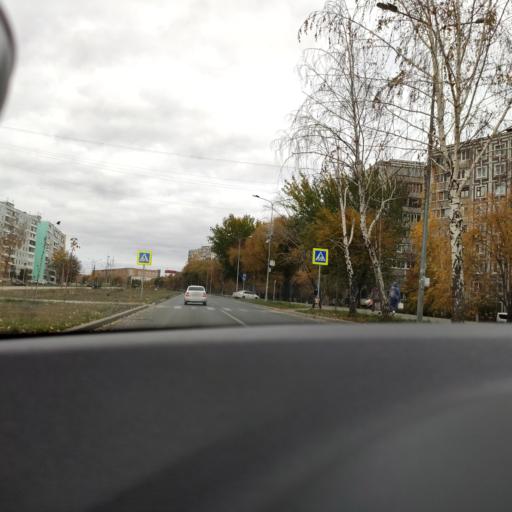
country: RU
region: Samara
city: Samara
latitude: 53.2514
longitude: 50.2475
